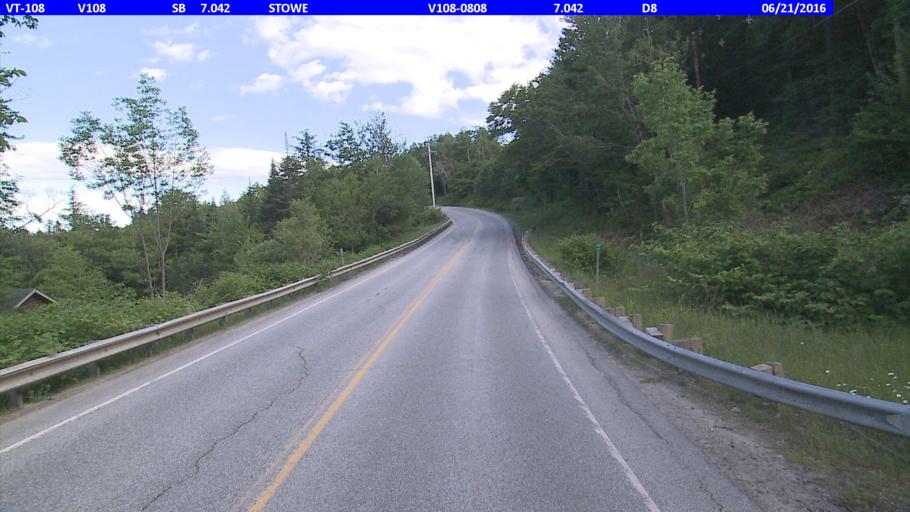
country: US
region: Vermont
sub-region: Lamoille County
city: Johnson
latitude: 44.5247
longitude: -72.7760
